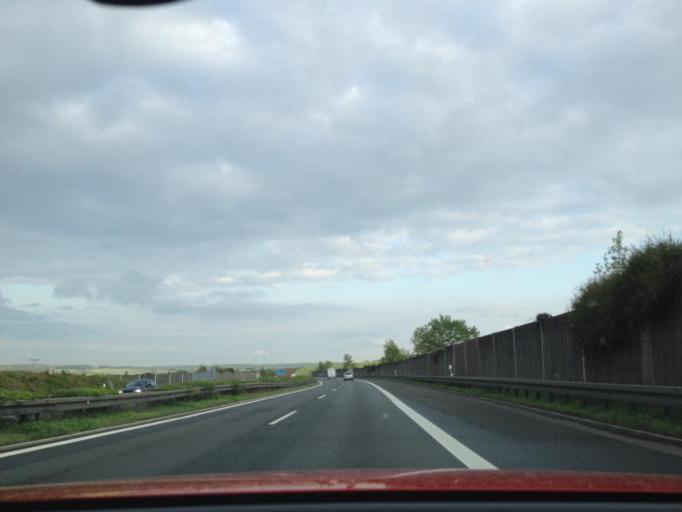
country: DE
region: Bavaria
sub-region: Upper Palatinate
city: Weiden
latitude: 49.6707
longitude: 12.1333
